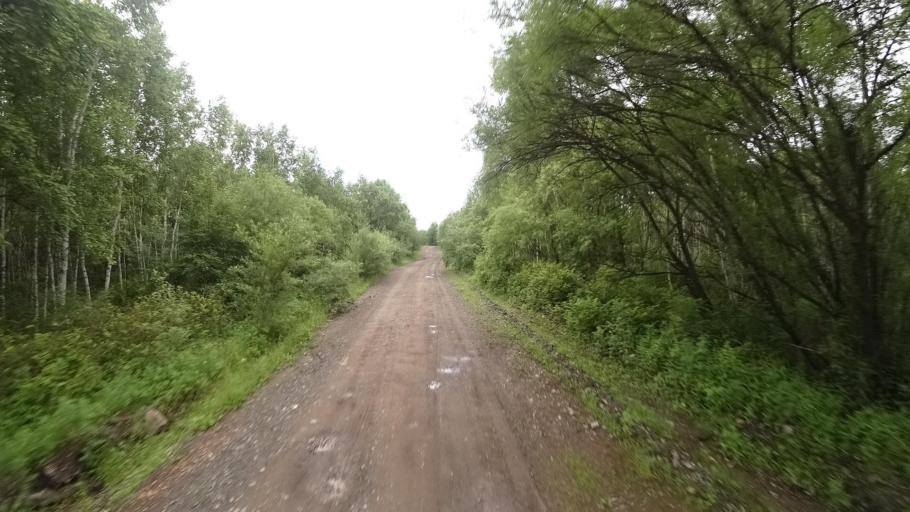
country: RU
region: Khabarovsk Krai
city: Amursk
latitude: 49.9139
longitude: 136.1592
